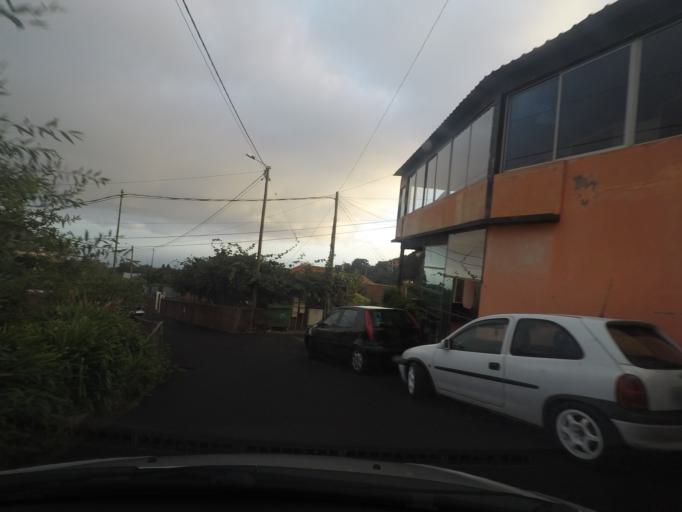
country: PT
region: Madeira
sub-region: Santa Cruz
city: Camacha
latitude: 32.6808
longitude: -16.8521
